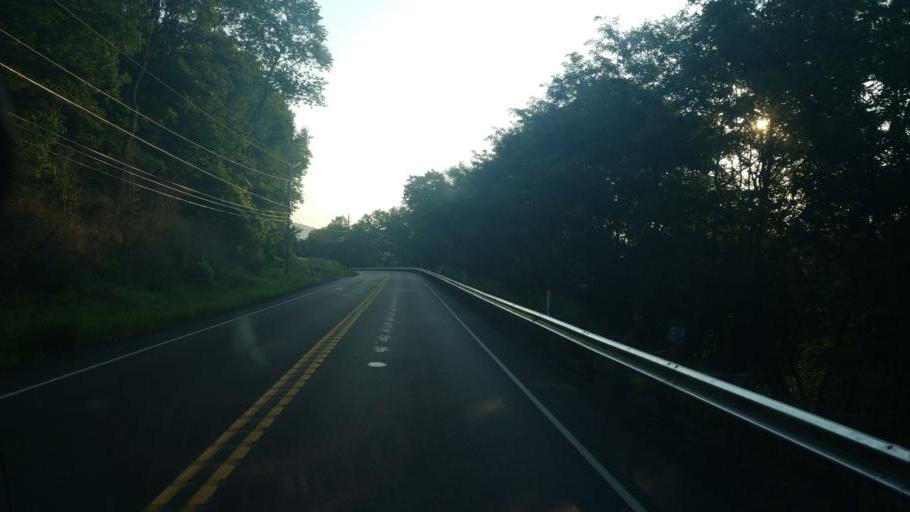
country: US
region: Pennsylvania
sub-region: Tioga County
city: Westfield
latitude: 41.9431
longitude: -77.4765
